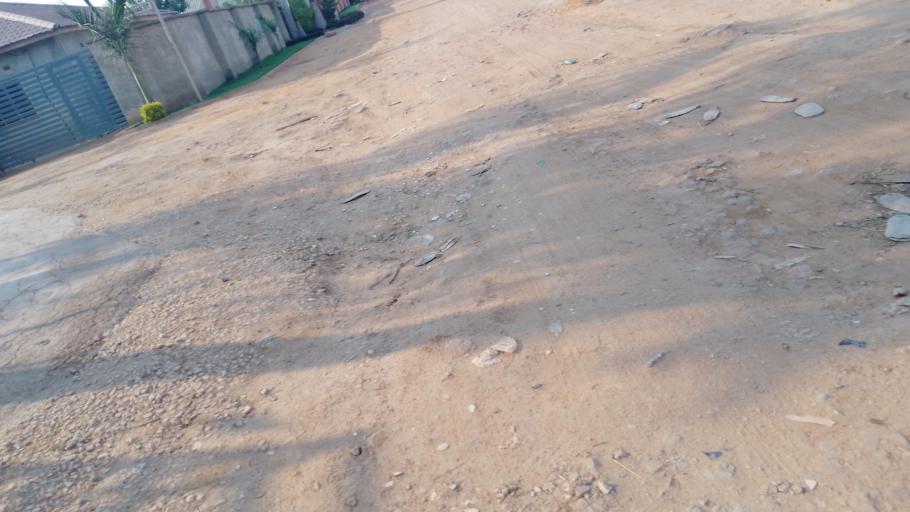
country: ZM
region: Lusaka
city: Lusaka
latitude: -15.3978
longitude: 28.3878
